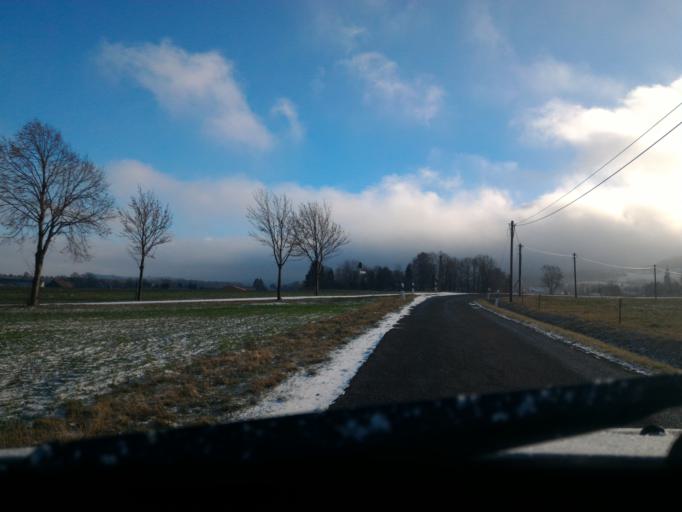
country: CZ
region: Ustecky
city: Varnsdorf
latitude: 50.8749
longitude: 14.6451
